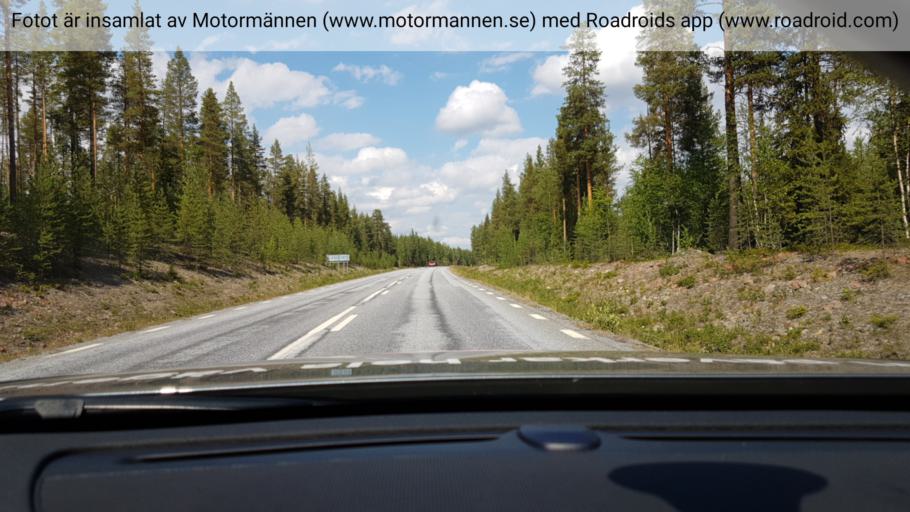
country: SE
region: Vaesterbotten
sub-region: Storumans Kommun
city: Storuman
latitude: 65.0711
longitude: 17.0997
